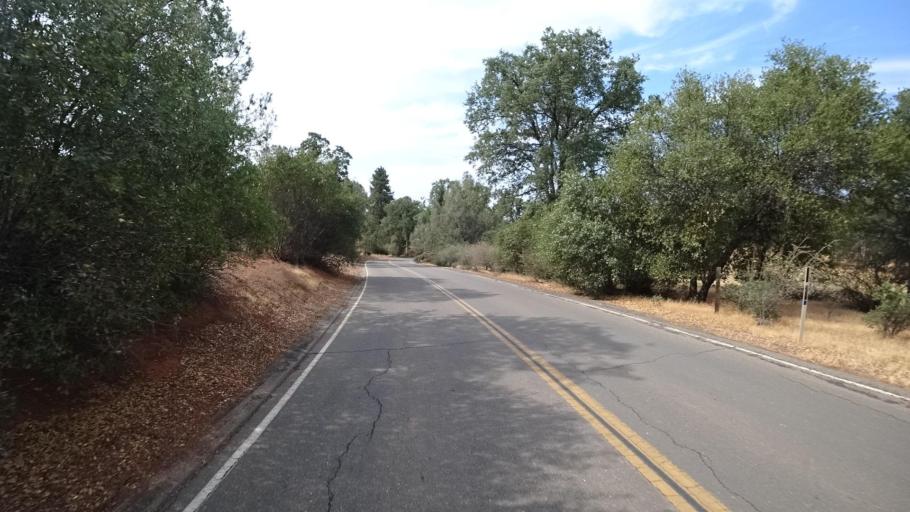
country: US
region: California
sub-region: Mariposa County
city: Midpines
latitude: 37.5377
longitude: -119.9712
